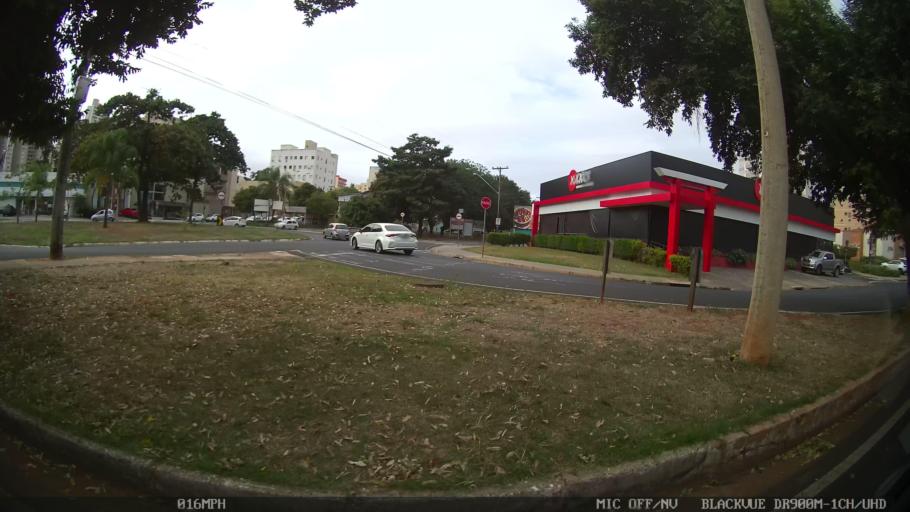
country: BR
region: Sao Paulo
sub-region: Sao Jose Do Rio Preto
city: Sao Jose do Rio Preto
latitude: -20.8302
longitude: -49.3862
